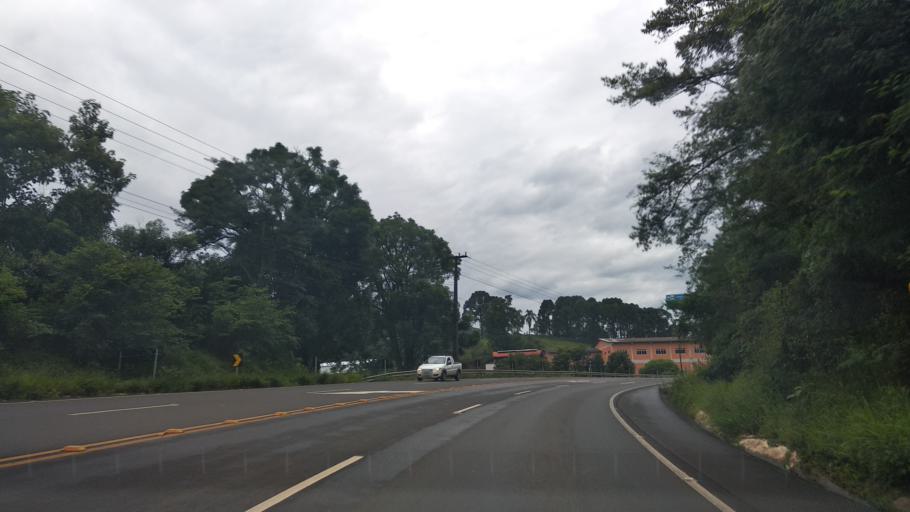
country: BR
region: Santa Catarina
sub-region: Videira
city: Videira
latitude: -27.0769
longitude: -51.2337
